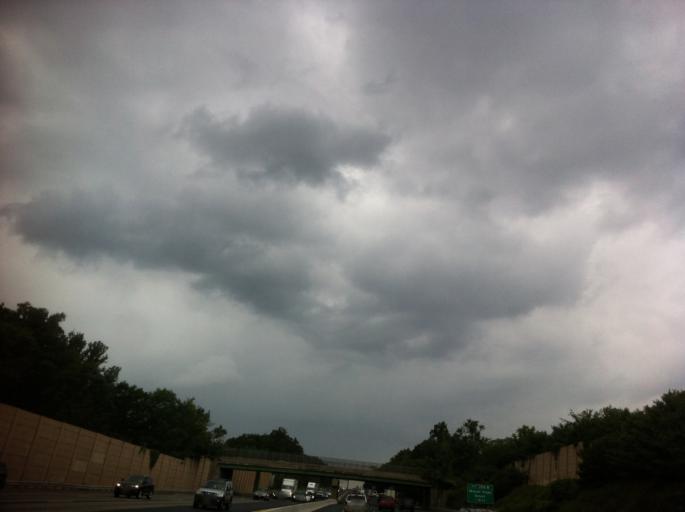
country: US
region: New Jersey
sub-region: Morris County
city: Mountain Lakes
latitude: 40.8884
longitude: -74.4739
